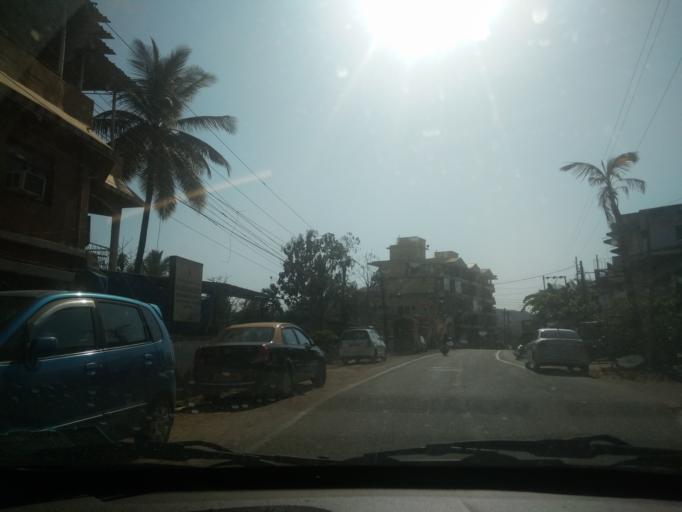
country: IN
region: Goa
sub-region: South Goa
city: Chicalim
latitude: 15.3883
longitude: 73.8493
